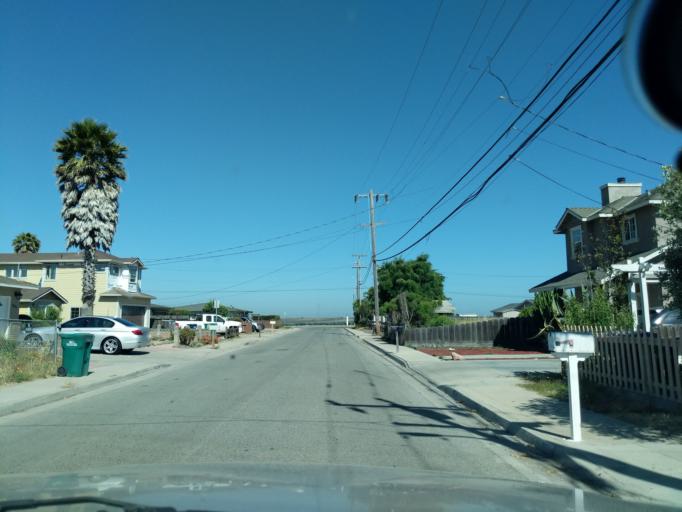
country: US
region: California
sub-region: Monterey County
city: Boronda
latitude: 36.6976
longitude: -121.6773
